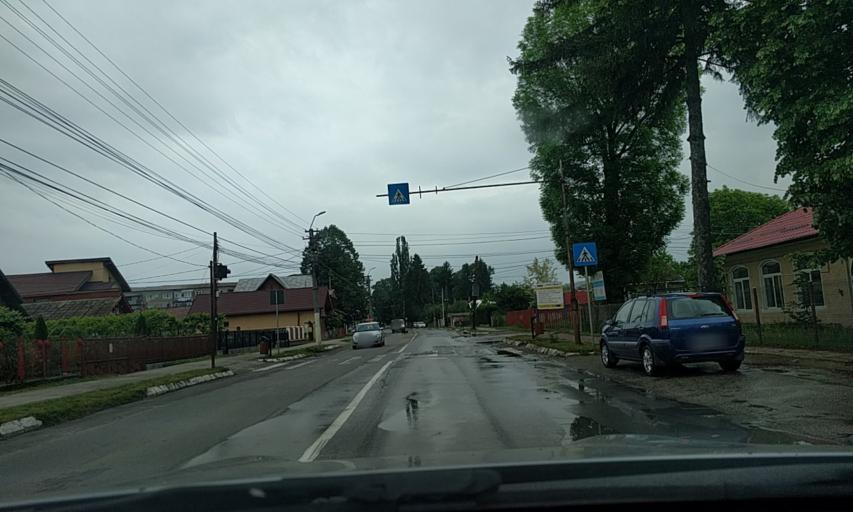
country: RO
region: Dambovita
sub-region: Oras Pucioasa
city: Glodeni
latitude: 45.0578
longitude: 25.4387
